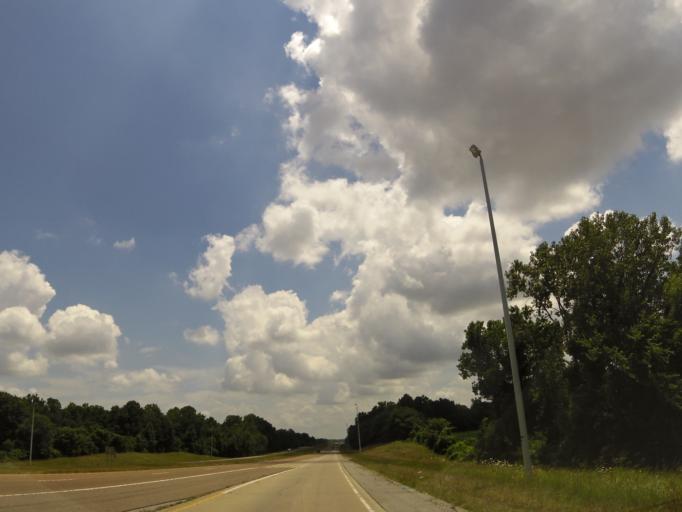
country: US
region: Tennessee
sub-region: Dyer County
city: Dyersburg
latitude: 36.0225
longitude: -89.3409
